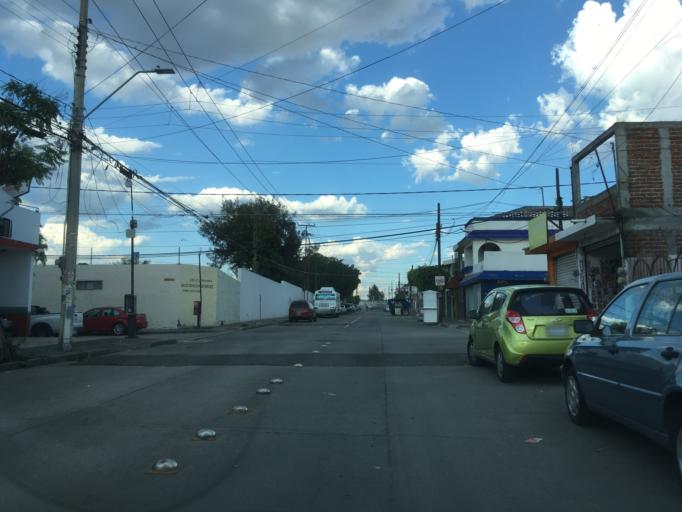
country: MX
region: Guanajuato
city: Leon
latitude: 21.0960
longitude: -101.6397
